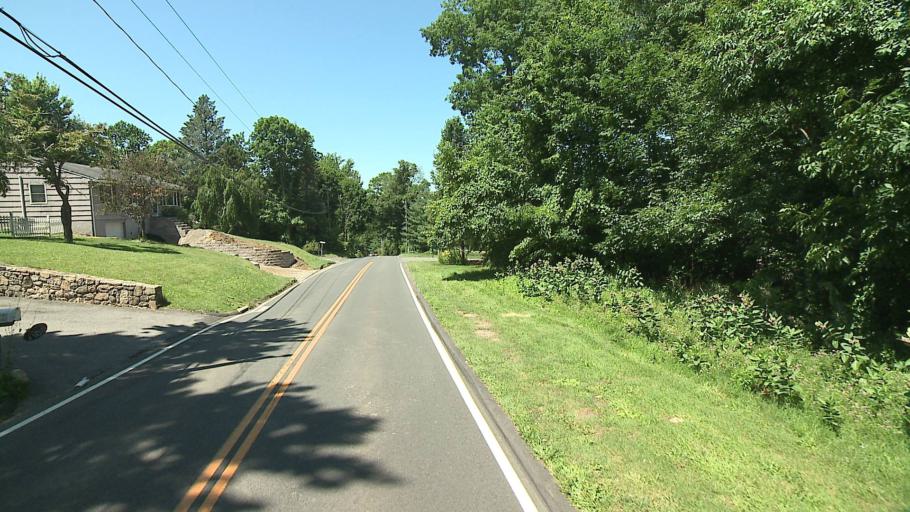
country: US
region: New York
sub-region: Putnam County
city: Putnam Lake
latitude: 41.4565
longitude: -73.5297
